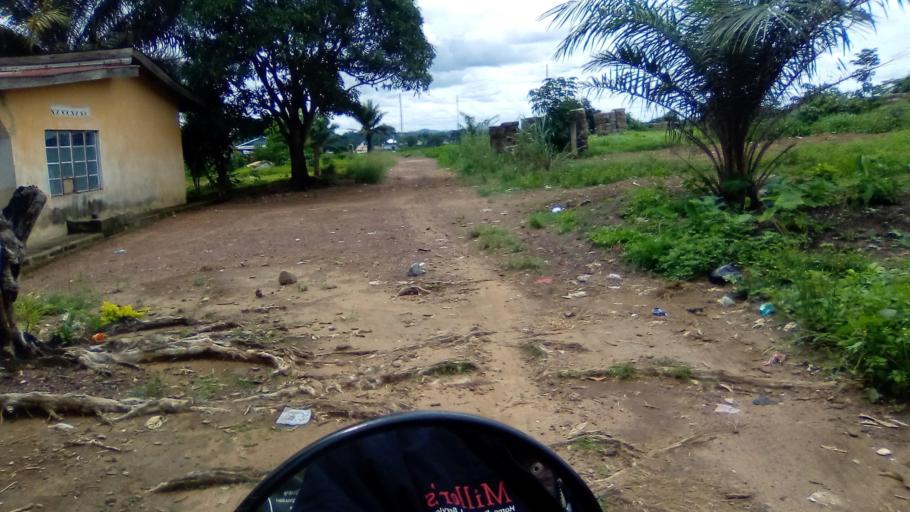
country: SL
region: Southern Province
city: Bo
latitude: 7.9339
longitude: -11.7209
